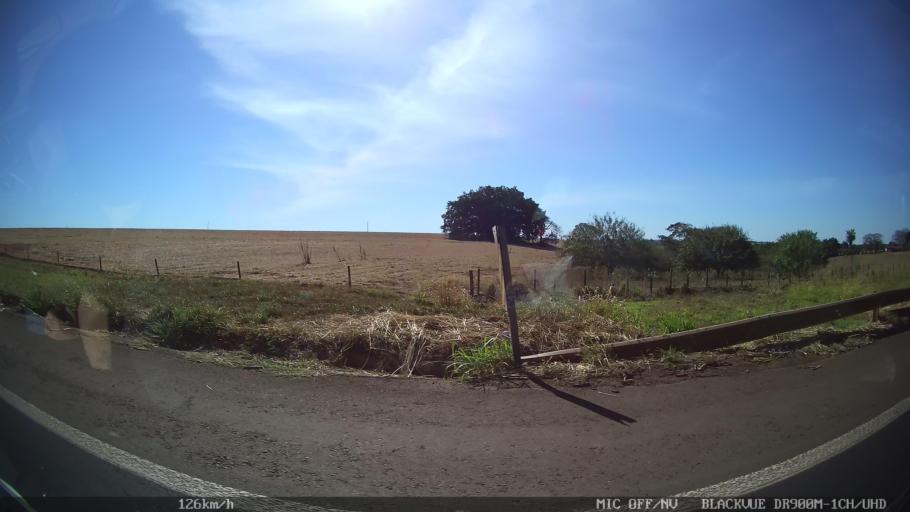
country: BR
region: Sao Paulo
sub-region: Olimpia
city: Olimpia
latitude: -20.6234
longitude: -48.7754
